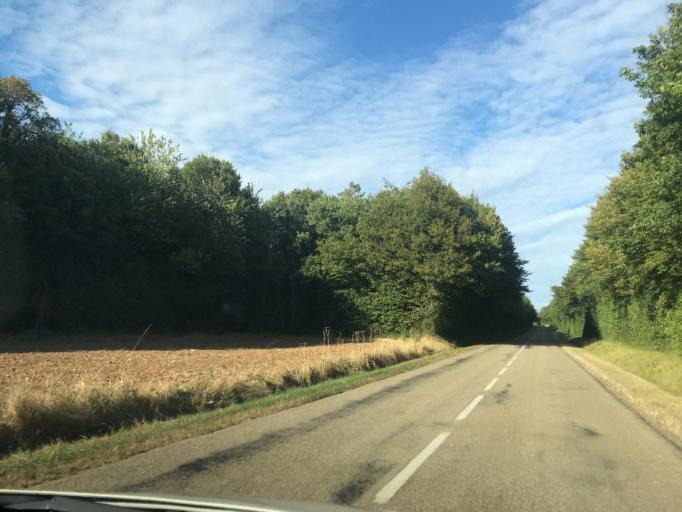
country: FR
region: Bourgogne
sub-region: Departement de l'Yonne
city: Fontenailles
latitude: 47.5666
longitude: 3.4460
